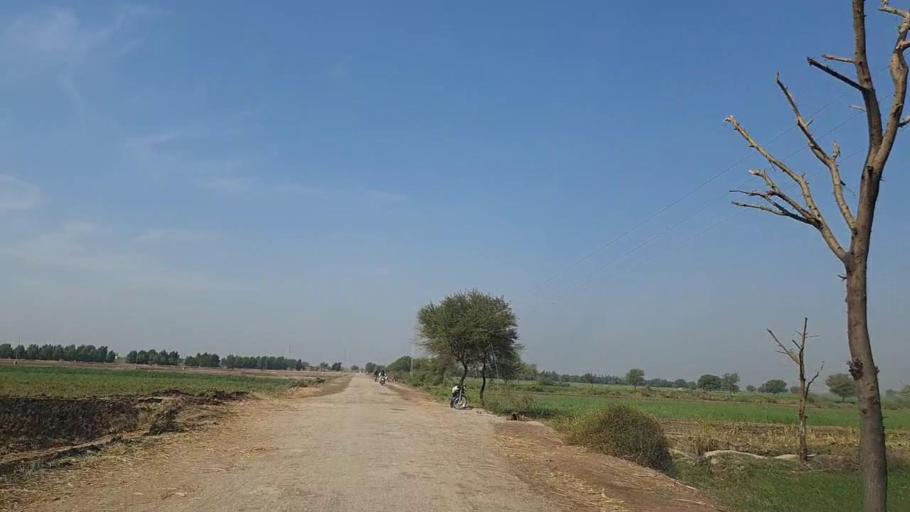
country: PK
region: Sindh
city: Mirpur Khas
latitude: 25.4825
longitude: 68.9862
